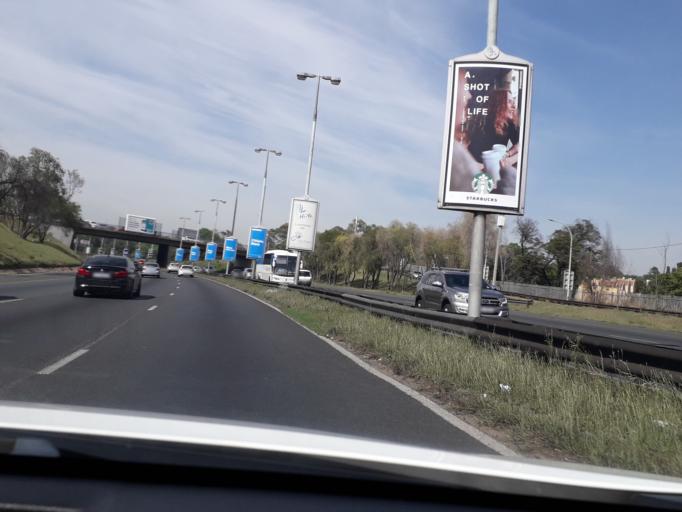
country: ZA
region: Gauteng
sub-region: City of Johannesburg Metropolitan Municipality
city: Johannesburg
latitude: -26.1450
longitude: 28.0593
